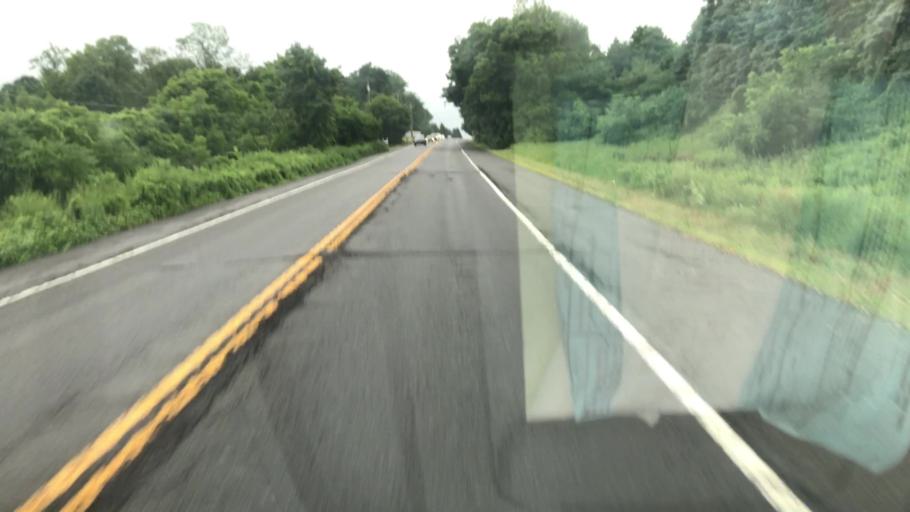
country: US
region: New York
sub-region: Onondaga County
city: Fayetteville
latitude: 43.0188
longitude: -76.0228
